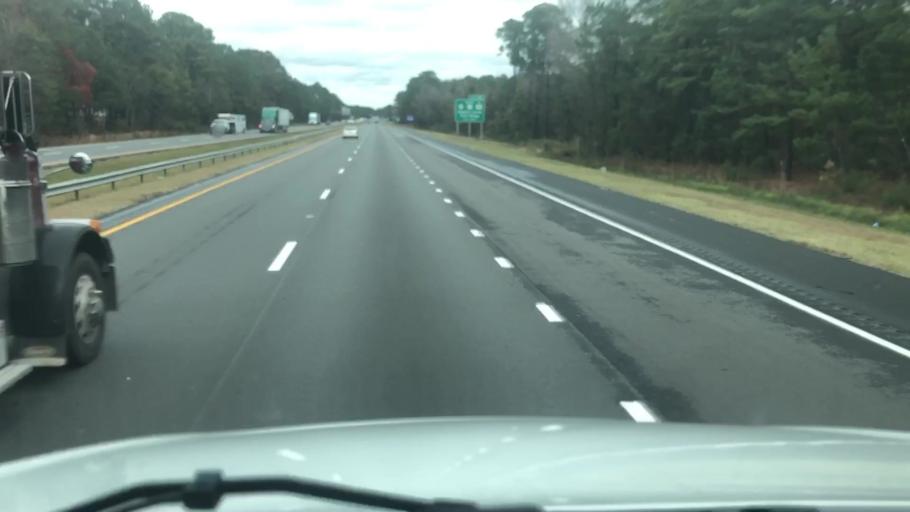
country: US
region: North Carolina
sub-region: Cumberland County
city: Eastover
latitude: 35.0992
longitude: -78.7750
